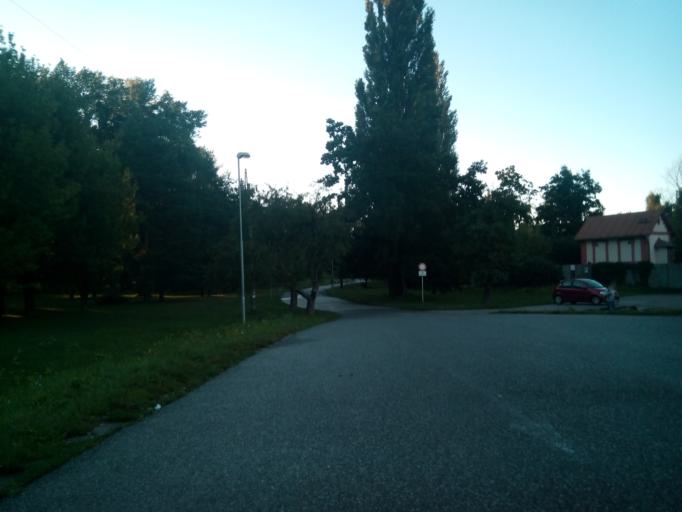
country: SK
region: Kosicky
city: Kosice
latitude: 48.7450
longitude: 21.2543
